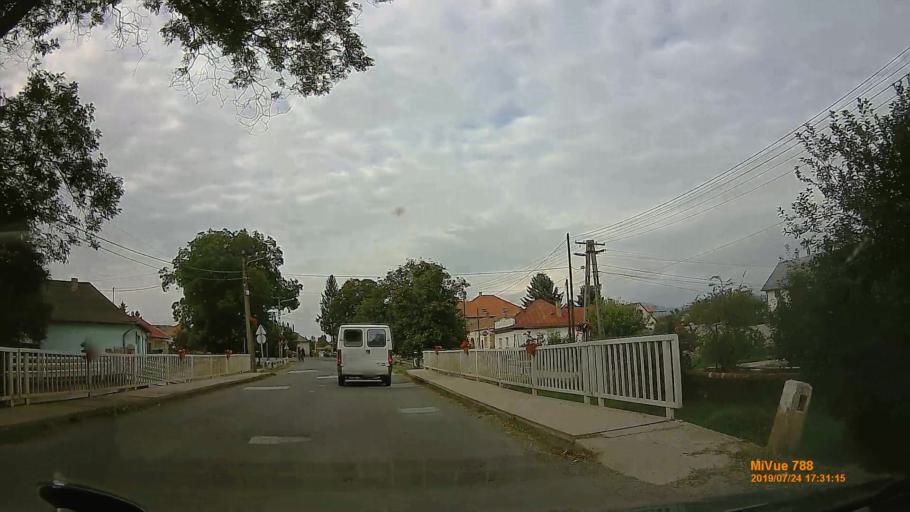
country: HU
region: Borsod-Abauj-Zemplen
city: Abaujszanto
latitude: 48.2823
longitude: 21.1872
